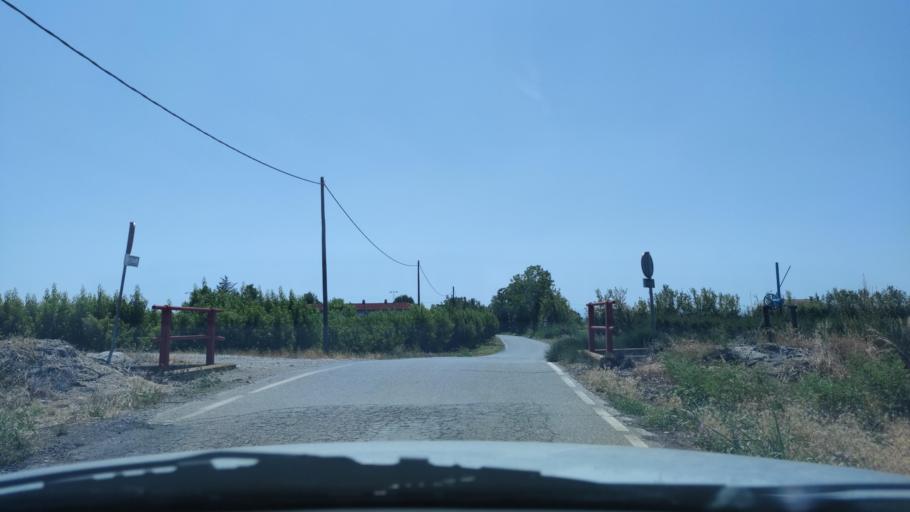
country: ES
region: Catalonia
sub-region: Provincia de Lleida
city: Torrefarrera
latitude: 41.6549
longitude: 0.5948
